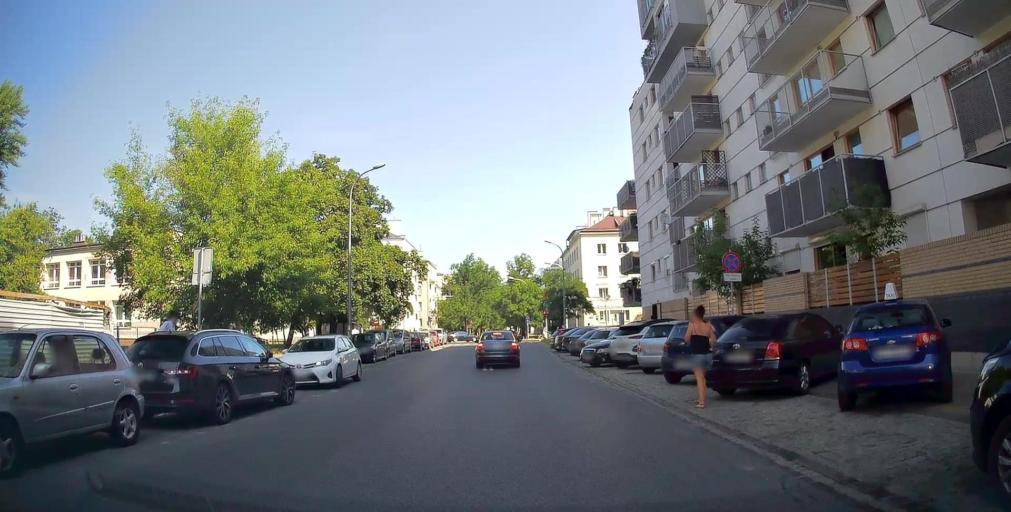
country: PL
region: Masovian Voivodeship
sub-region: Warszawa
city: Mokotow
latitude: 52.2016
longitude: 21.0461
